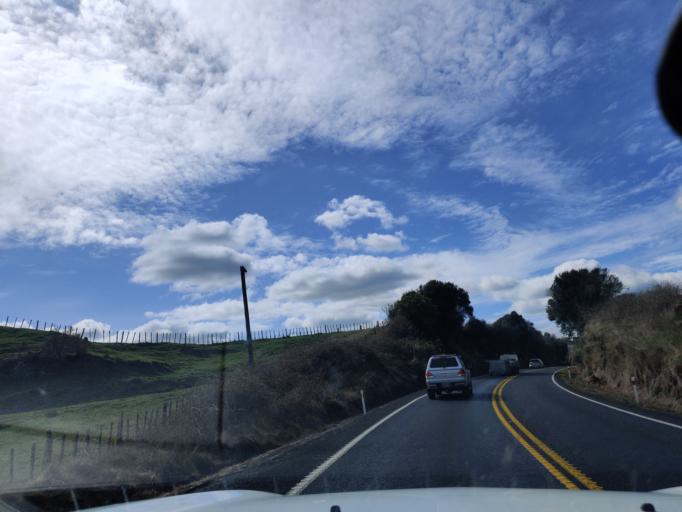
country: NZ
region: Waikato
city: Turangi
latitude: -39.0655
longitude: 175.3712
